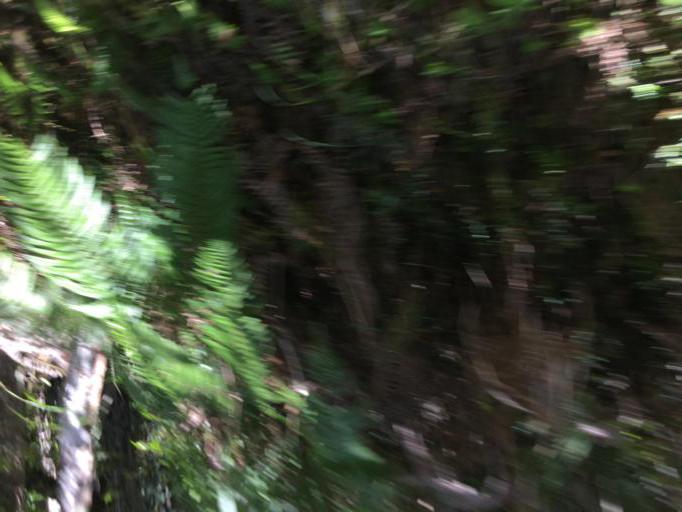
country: TW
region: Taiwan
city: Daxi
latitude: 24.5360
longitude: 121.4020
